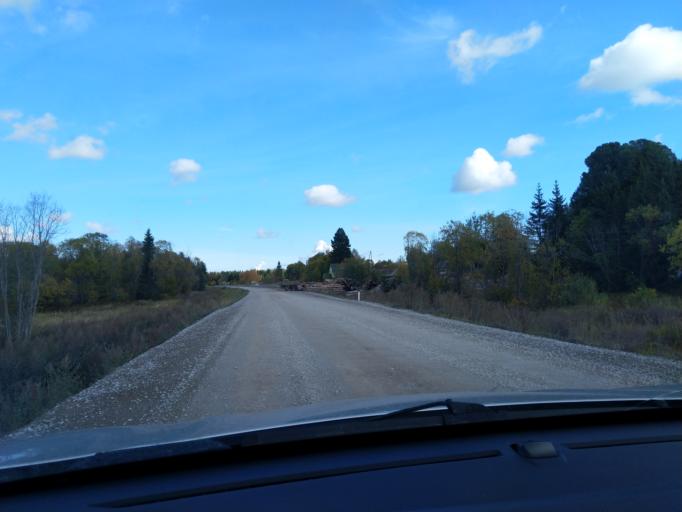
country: RU
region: Perm
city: Usol'ye
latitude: 59.4618
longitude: 56.3619
